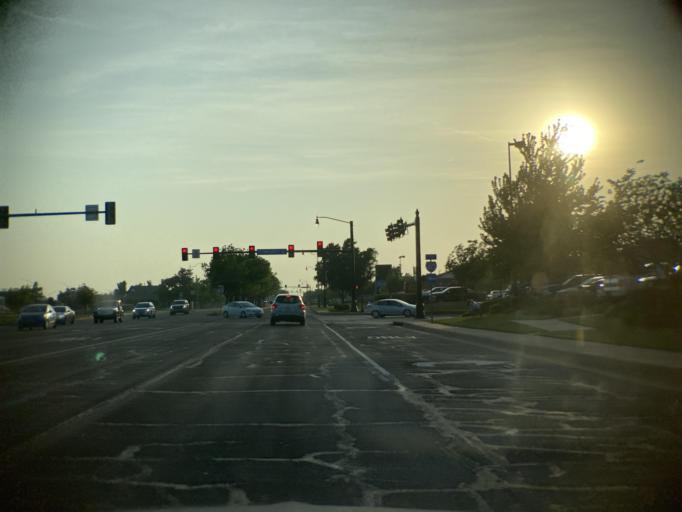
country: US
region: Oklahoma
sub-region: Oklahoma County
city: Midwest City
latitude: 35.4353
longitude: -97.3964
